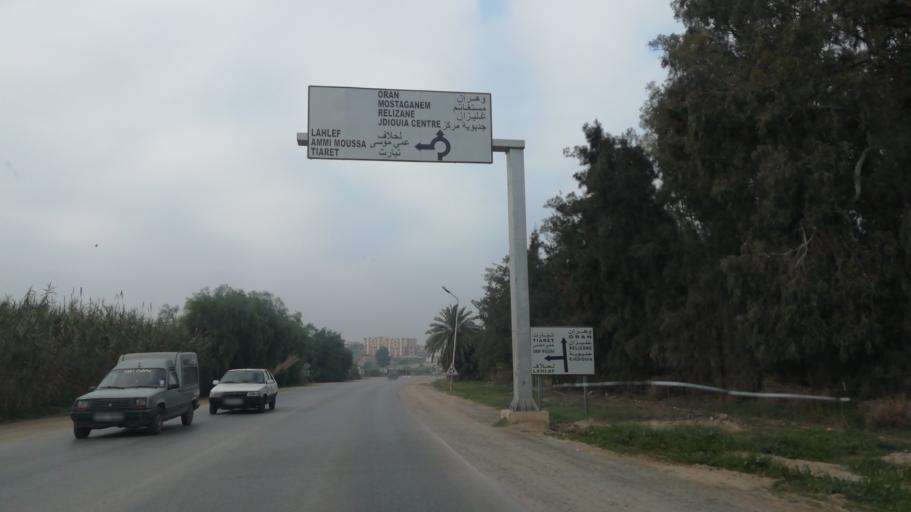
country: DZ
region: Relizane
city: Djidiouia
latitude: 35.9315
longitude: 0.8471
